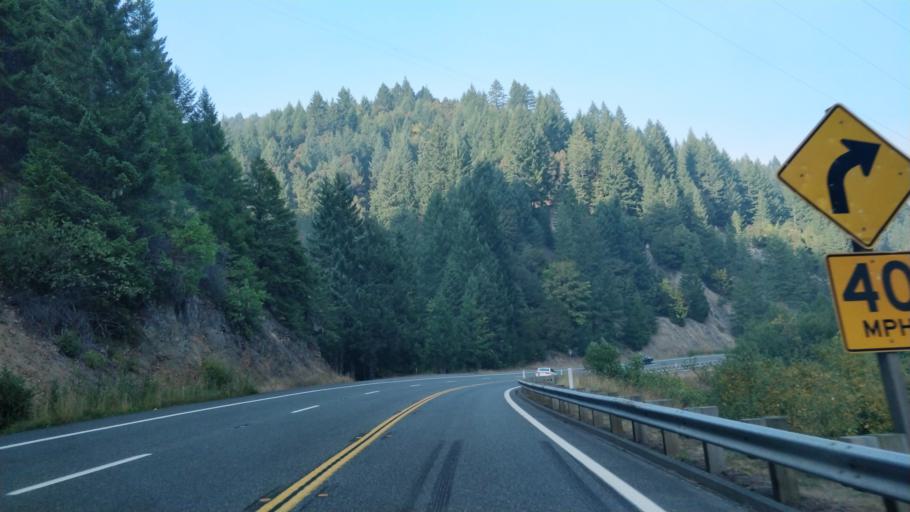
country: US
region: California
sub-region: Humboldt County
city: Willow Creek
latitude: 40.9015
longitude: -123.7673
